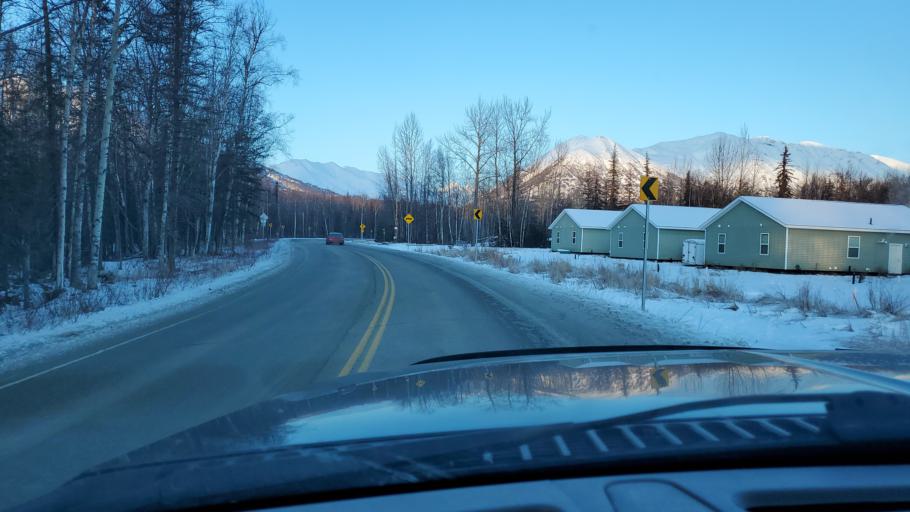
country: US
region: Alaska
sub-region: Matanuska-Susitna Borough
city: Fishhook
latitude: 61.6851
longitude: -149.2463
